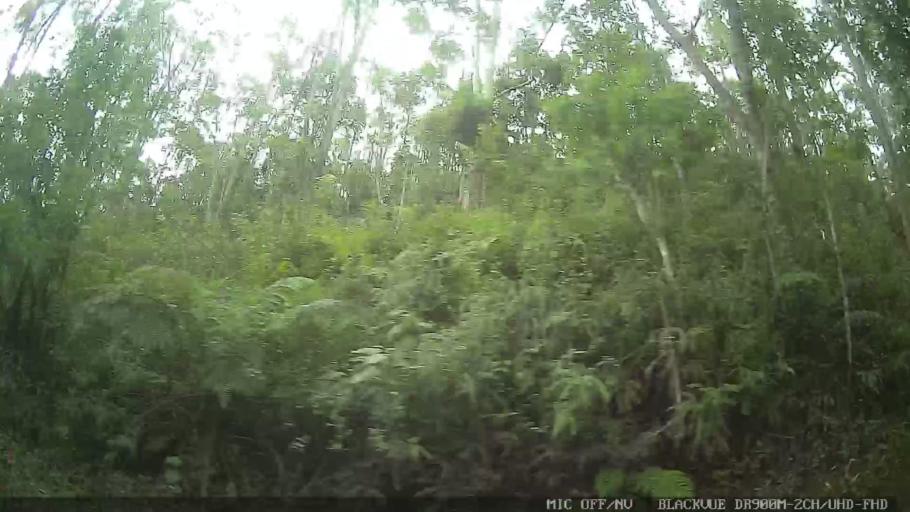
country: BR
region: Sao Paulo
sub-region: Santa Branca
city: Santa Branca
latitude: -23.5285
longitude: -45.7287
